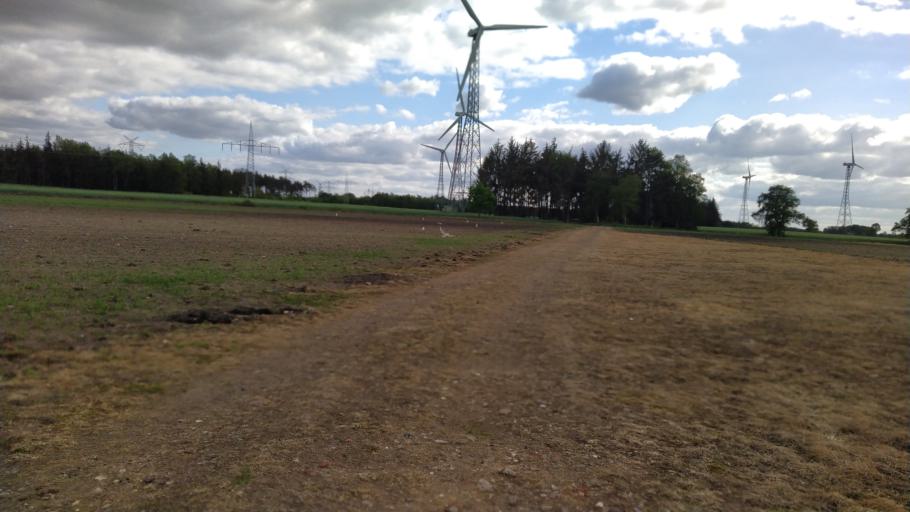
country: DE
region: Lower Saxony
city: Brest
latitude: 53.4390
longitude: 9.3940
